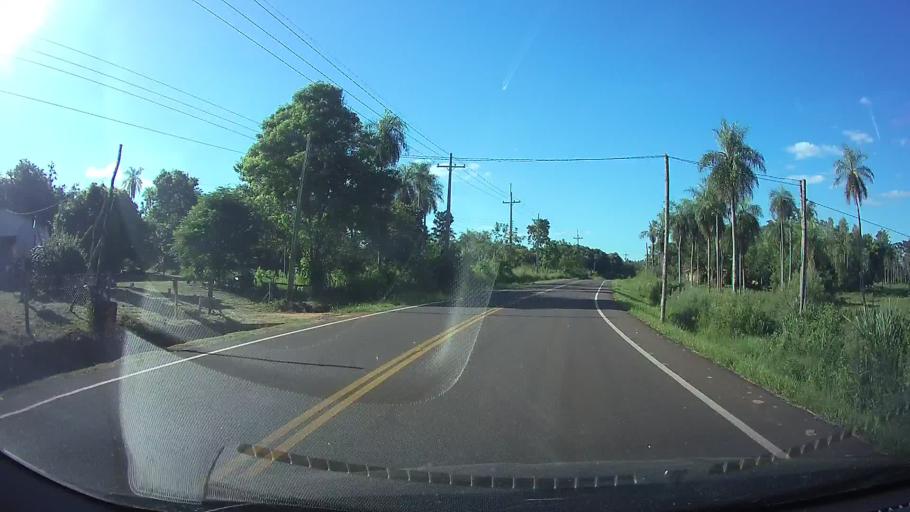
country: PY
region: Cordillera
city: Caacupe
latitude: -25.3436
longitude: -57.1540
